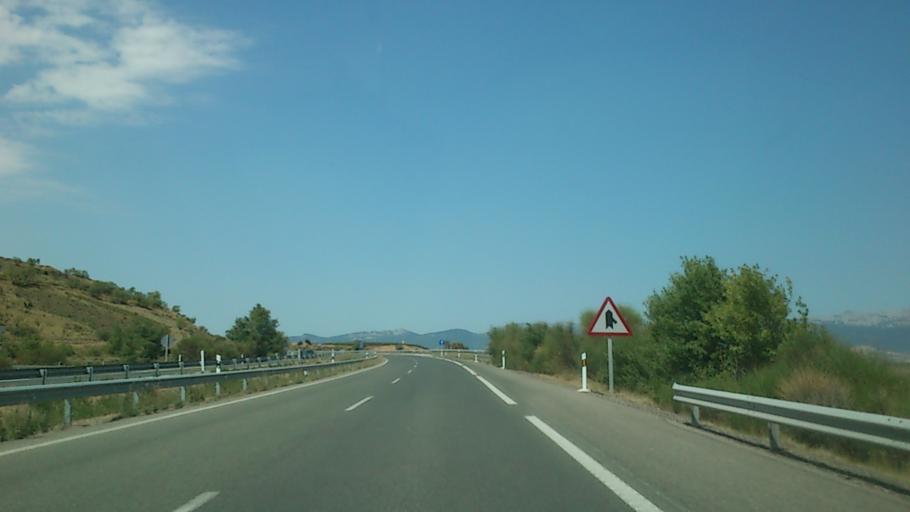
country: ES
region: La Rioja
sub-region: Provincia de La Rioja
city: Cenicero
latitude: 42.4691
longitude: -2.6461
